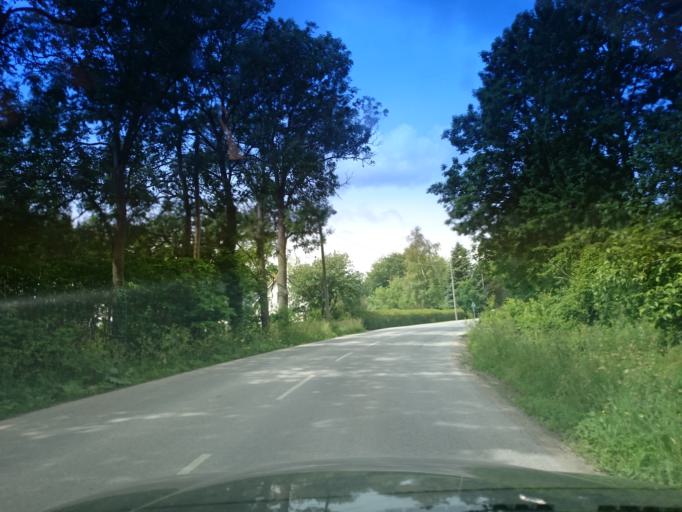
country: SE
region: Gotland
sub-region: Gotland
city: Hemse
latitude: 57.2572
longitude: 18.6344
